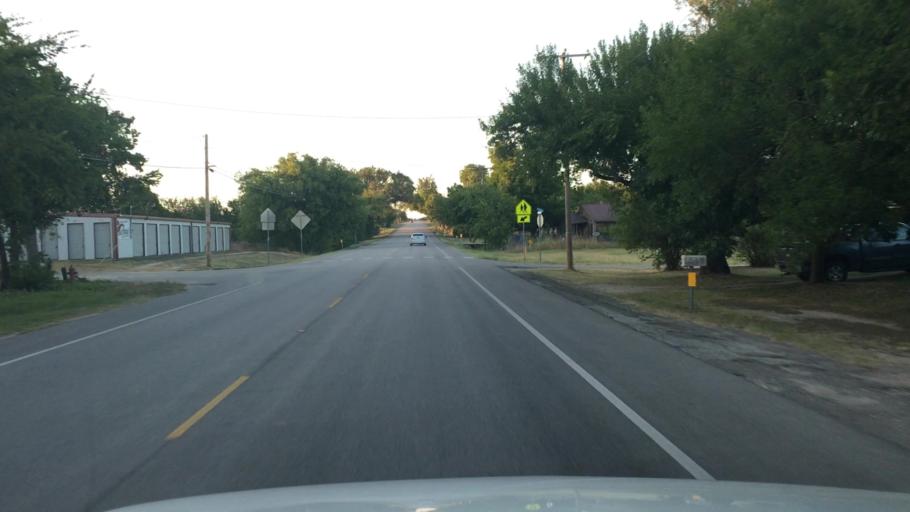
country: US
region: Texas
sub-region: Hamilton County
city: Hico
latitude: 31.9857
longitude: -98.0275
